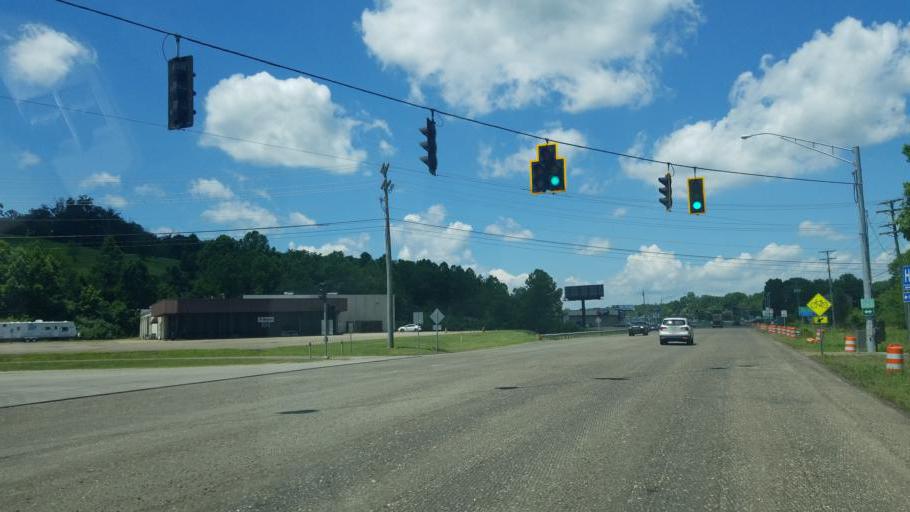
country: US
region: Ohio
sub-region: Gallia County
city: Gallipolis
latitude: 38.8438
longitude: -82.2312
